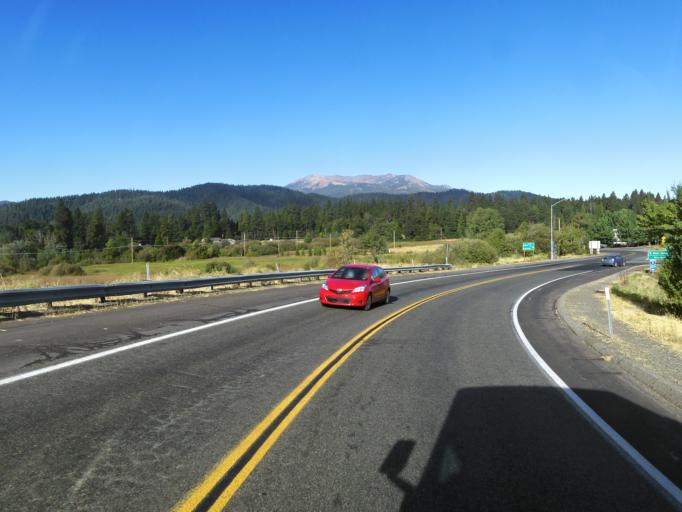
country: US
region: California
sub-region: Siskiyou County
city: Mount Shasta
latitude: 41.3099
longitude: -122.3213
